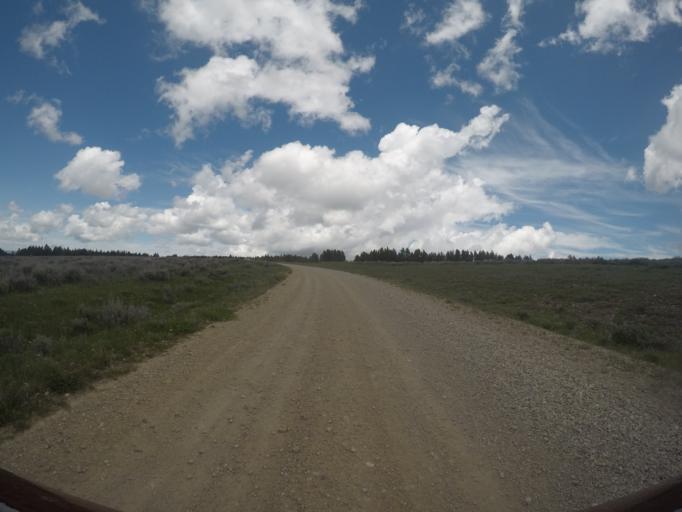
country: US
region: Wyoming
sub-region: Big Horn County
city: Lovell
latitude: 45.1723
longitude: -108.4519
